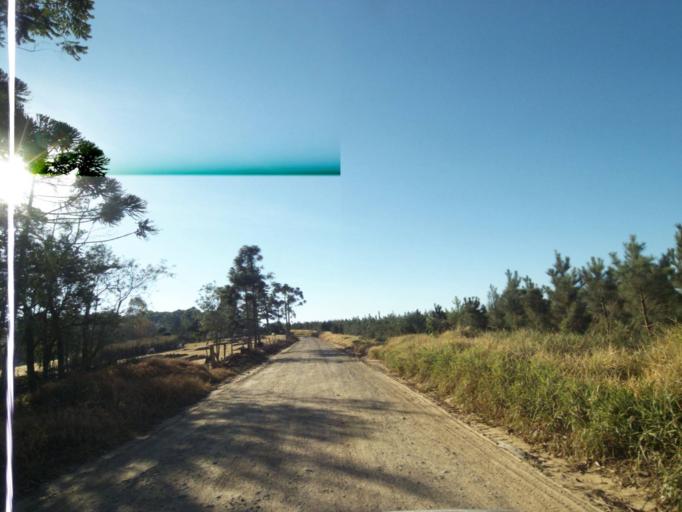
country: BR
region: Parana
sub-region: Telemaco Borba
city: Telemaco Borba
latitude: -24.5168
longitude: -50.6476
